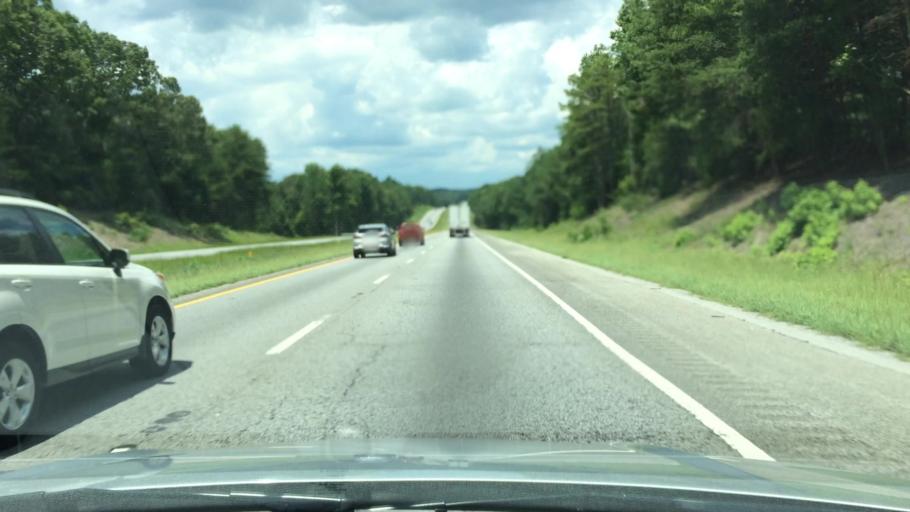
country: US
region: South Carolina
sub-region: Spartanburg County
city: Woodruff
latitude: 34.7201
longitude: -81.9459
